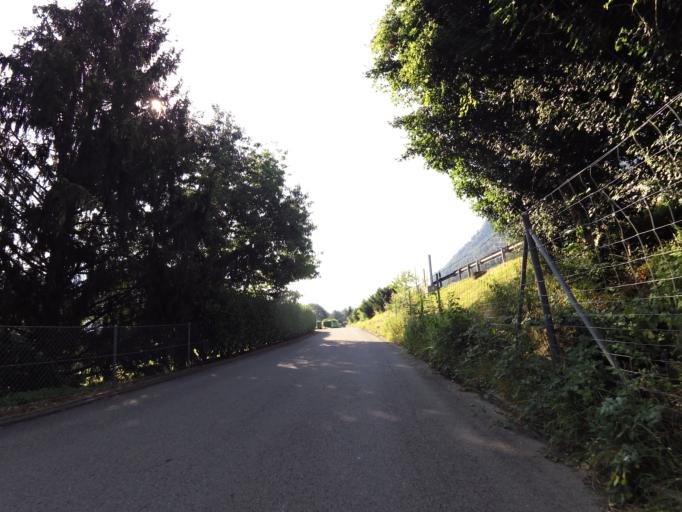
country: CH
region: Schwyz
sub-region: Bezirk Kuessnacht
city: Kussnacht
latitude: 47.0833
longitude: 8.4793
